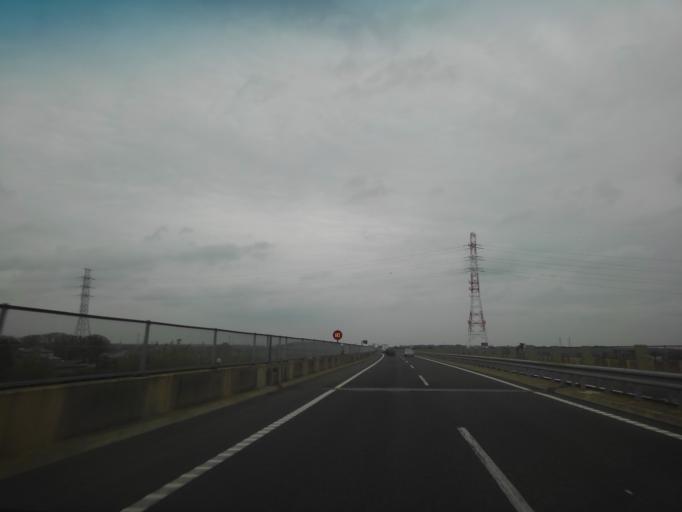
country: JP
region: Chiba
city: Kisarazu
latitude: 35.3979
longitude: 139.9678
